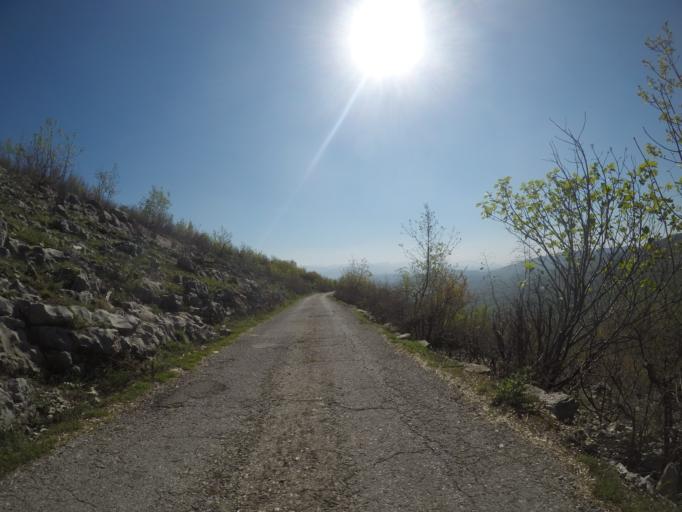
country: ME
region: Danilovgrad
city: Danilovgrad
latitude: 42.5151
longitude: 19.0700
